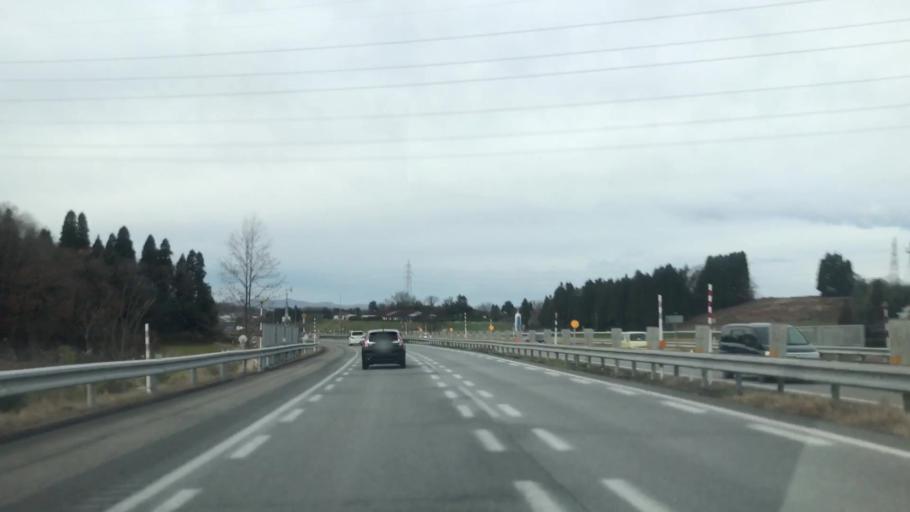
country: JP
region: Toyama
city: Kuragaki-kosugi
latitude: 36.6899
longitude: 137.0967
